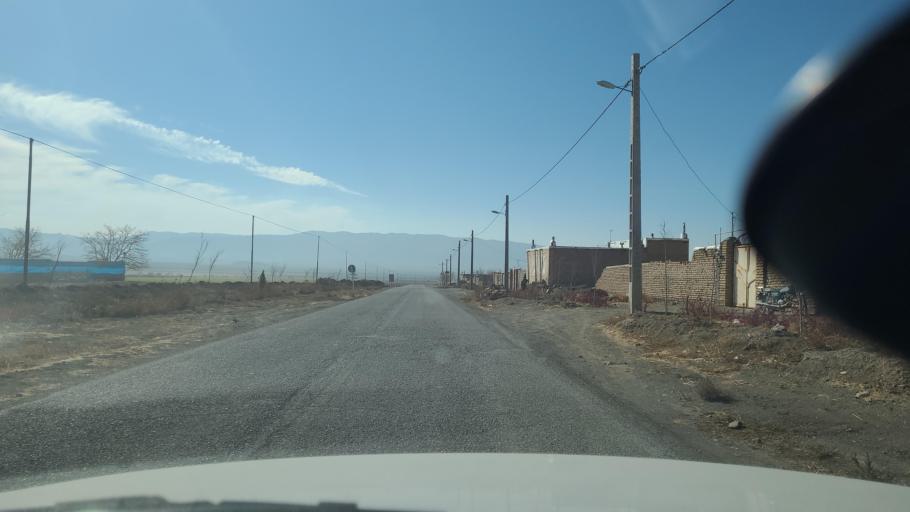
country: IR
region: Razavi Khorasan
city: Dowlatabad
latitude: 35.6178
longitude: 59.4756
